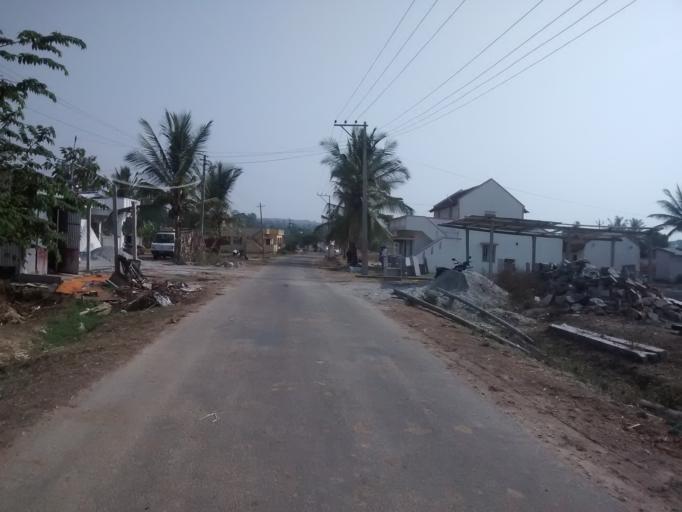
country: IN
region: Karnataka
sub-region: Hassan
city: Hassan
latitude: 12.9345
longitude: 76.1606
